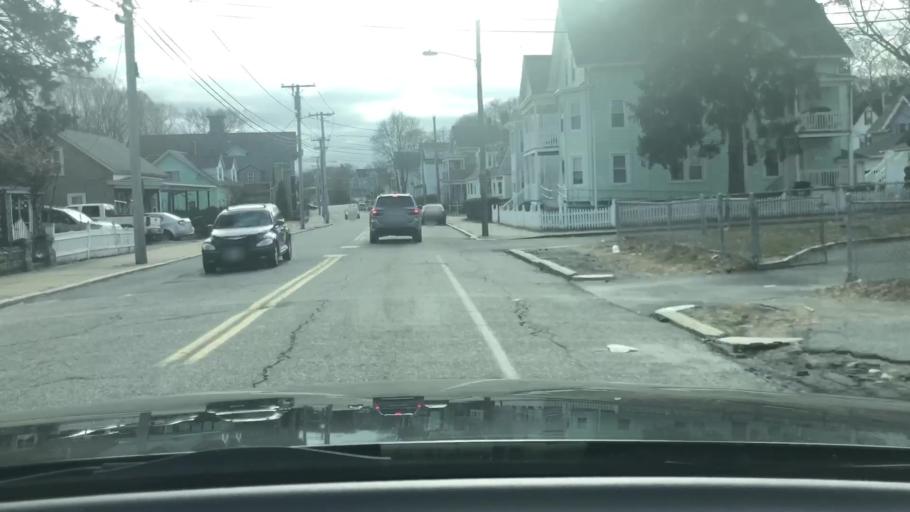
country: US
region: Rhode Island
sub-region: Providence County
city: Woonsocket
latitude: 42.0123
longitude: -71.5141
